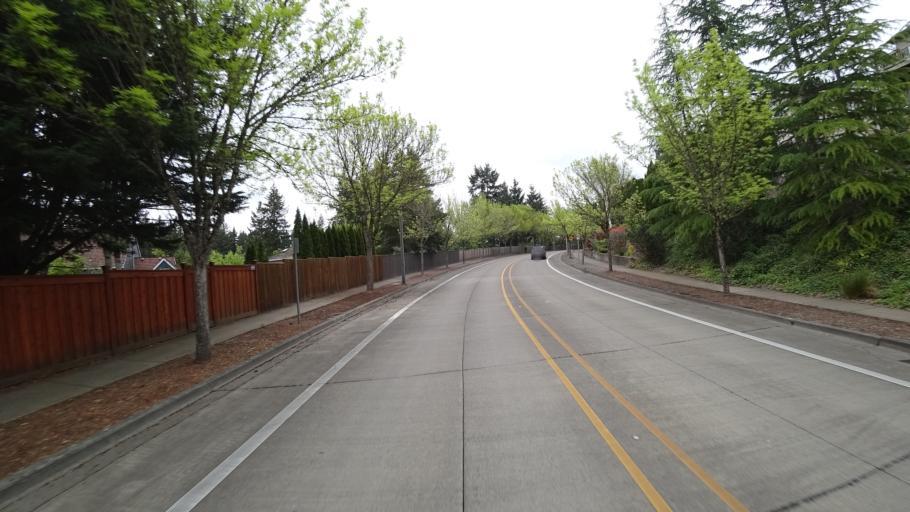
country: US
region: Oregon
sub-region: Washington County
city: Beaverton
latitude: 45.4600
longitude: -122.8317
